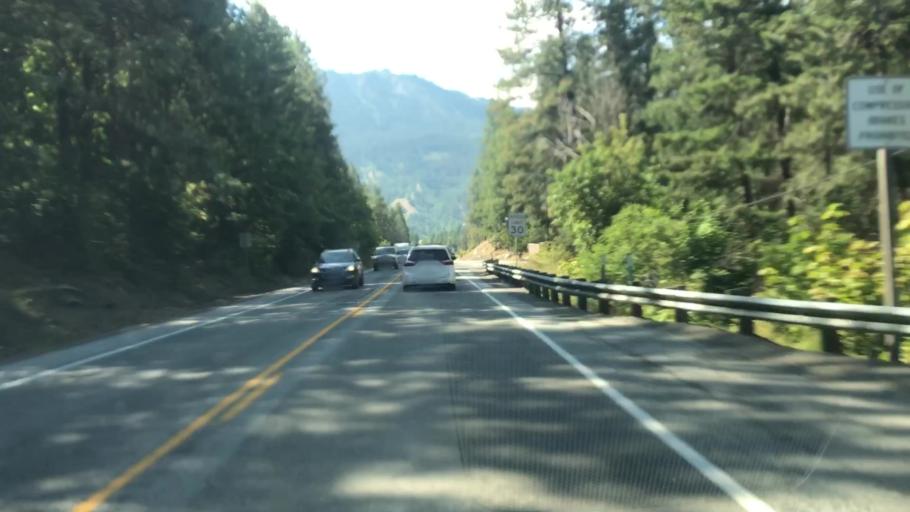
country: US
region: Washington
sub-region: Chelan County
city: Leavenworth
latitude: 47.5948
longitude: -120.6419
